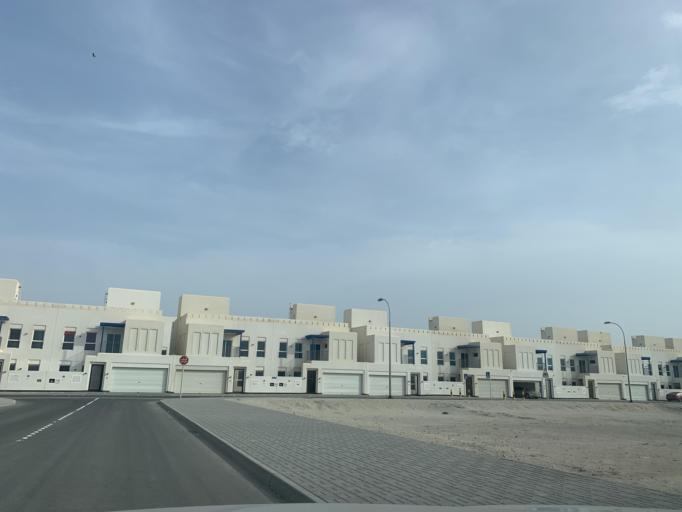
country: BH
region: Muharraq
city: Al Muharraq
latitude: 26.3157
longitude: 50.6280
